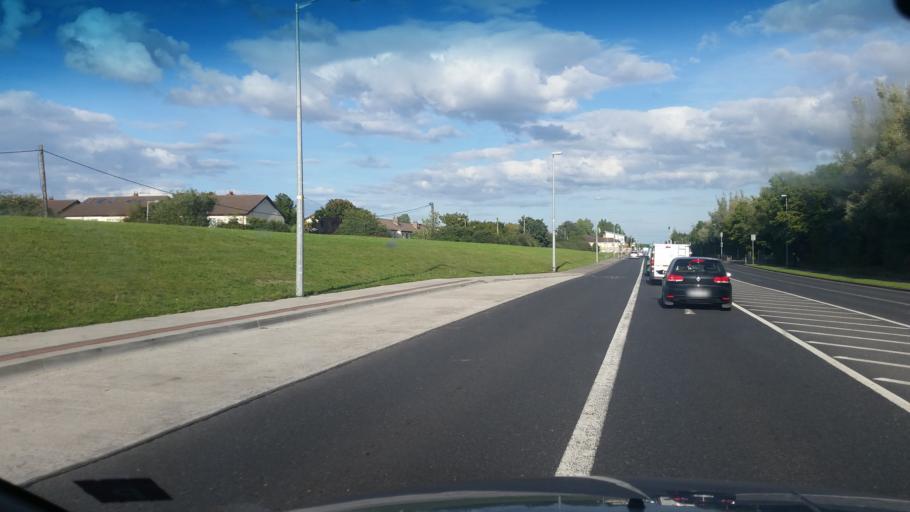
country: IE
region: Leinster
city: Beaumont
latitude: 53.3971
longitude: -6.2352
